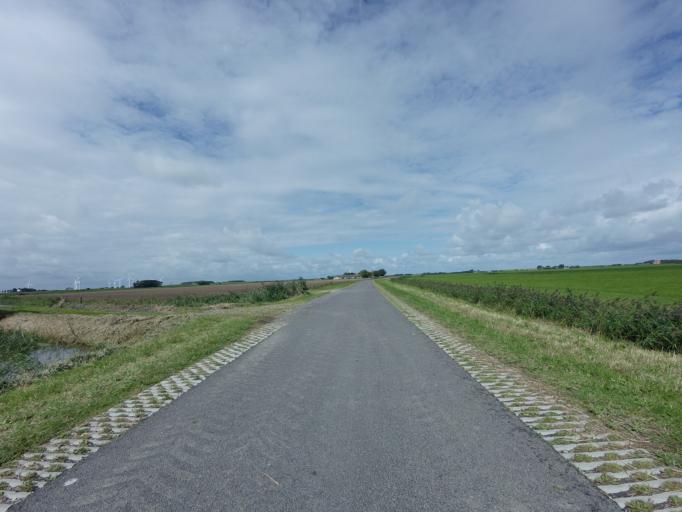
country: NL
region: Friesland
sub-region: Sudwest Fryslan
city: Makkum
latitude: 53.0968
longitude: 5.4187
